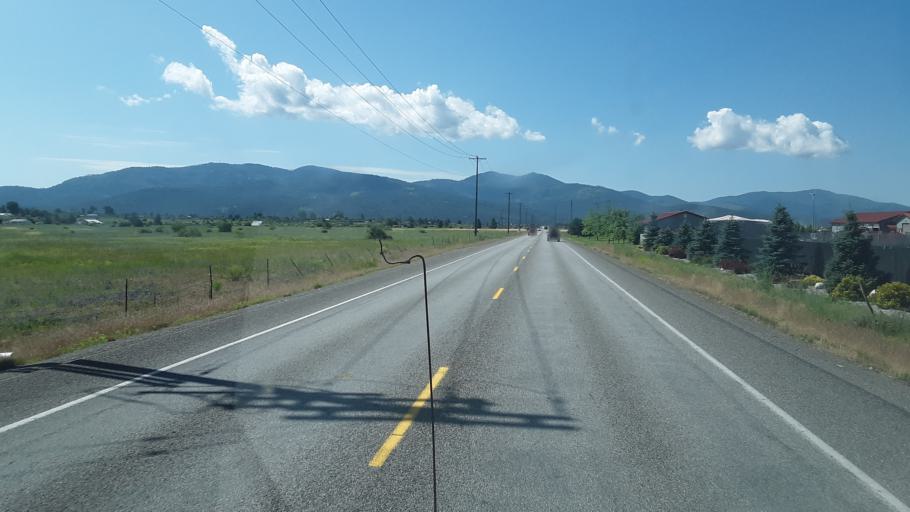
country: US
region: Idaho
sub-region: Kootenai County
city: Post Falls
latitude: 47.7373
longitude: -117.0019
